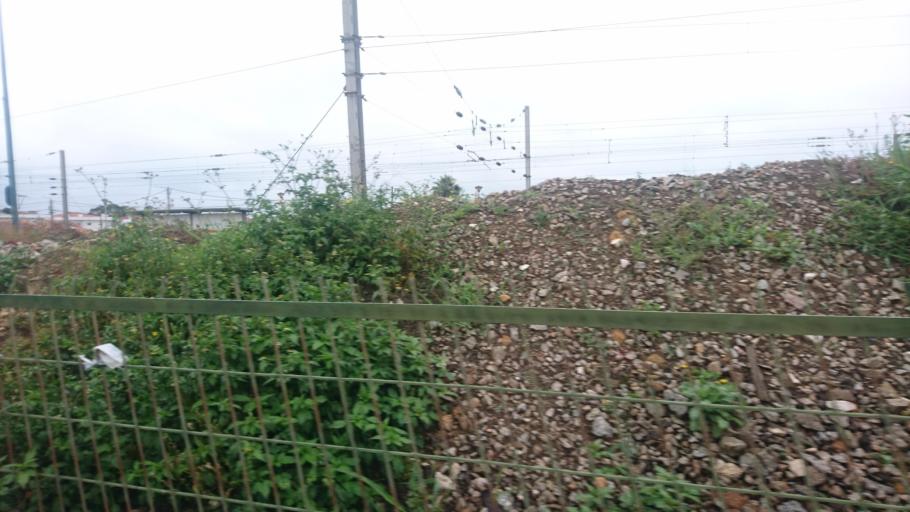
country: PT
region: Aveiro
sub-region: Ovar
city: Esmoriz
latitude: 40.9641
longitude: -8.6352
